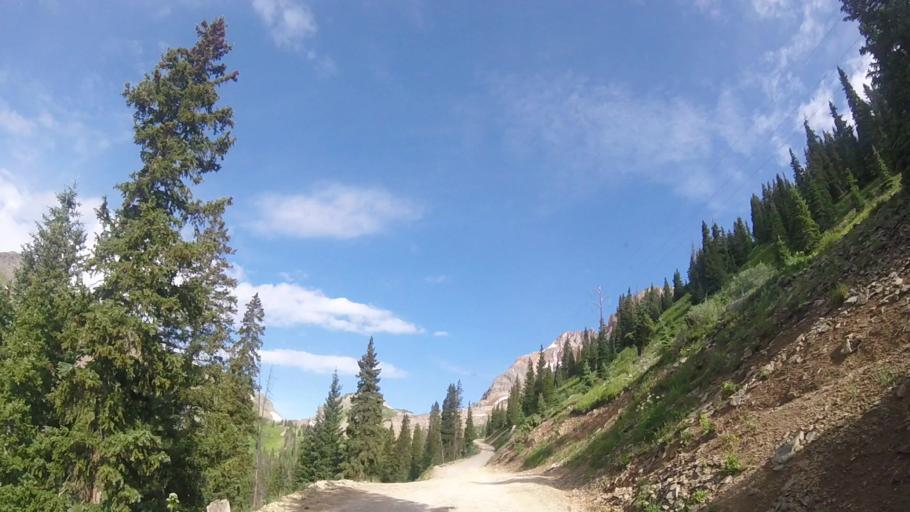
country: US
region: Colorado
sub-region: San Miguel County
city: Telluride
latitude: 37.8485
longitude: -107.7680
